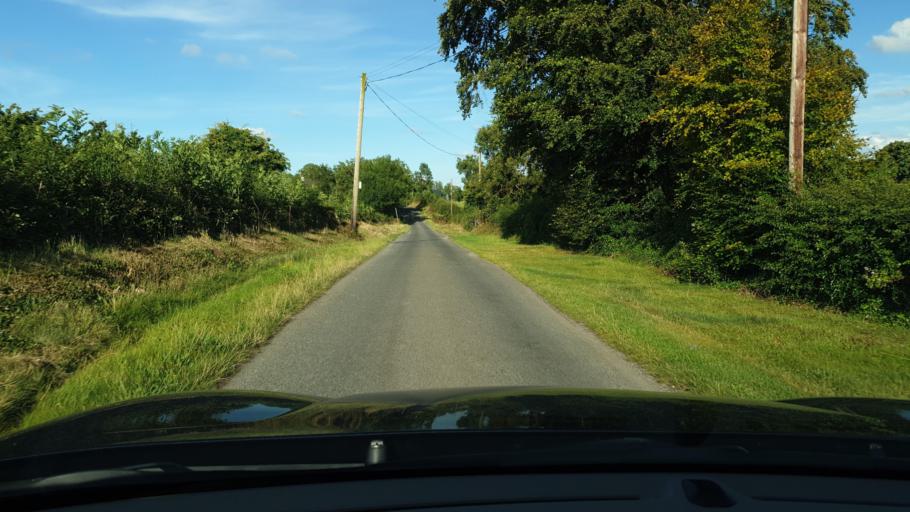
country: IE
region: Leinster
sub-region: An Mhi
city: Stamullin
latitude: 53.6084
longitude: -6.2786
